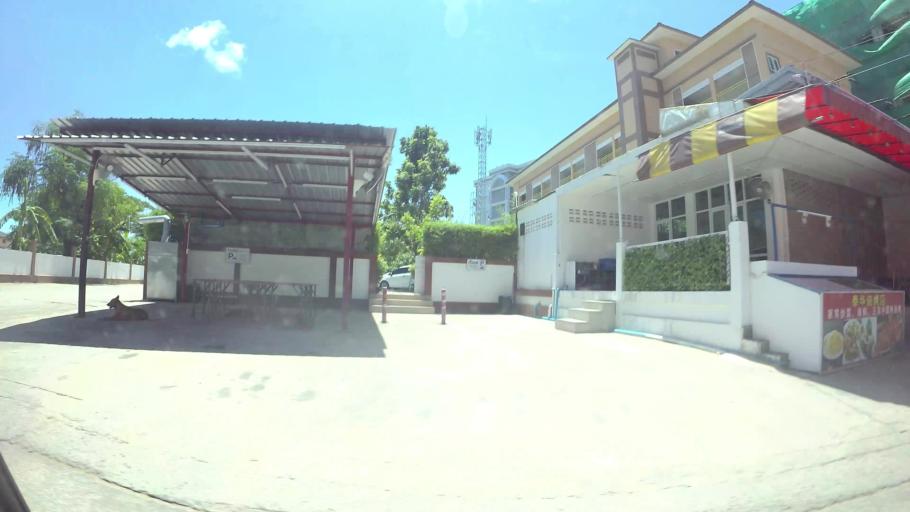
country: TH
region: Chon Buri
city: Phatthaya
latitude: 12.9205
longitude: 100.8927
